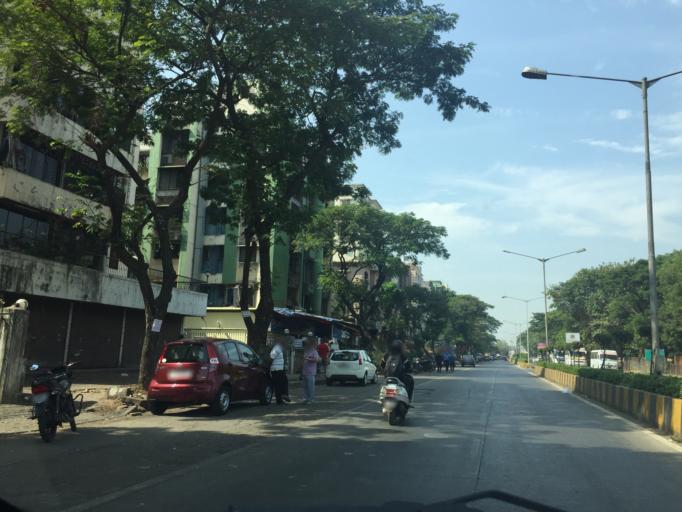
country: IN
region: Maharashtra
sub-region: Mumbai Suburban
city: Borivli
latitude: 19.2326
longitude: 72.8279
